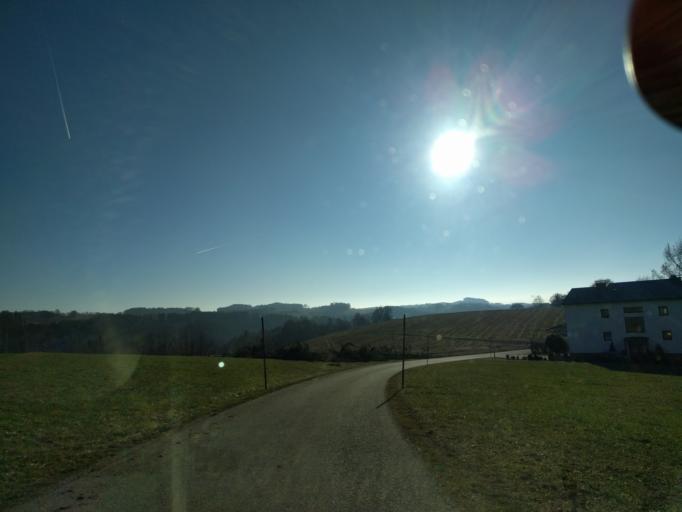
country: AT
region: Upper Austria
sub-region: Politischer Bezirk Urfahr-Umgebung
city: Kirchschlag bei Linz
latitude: 48.3954
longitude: 14.2897
